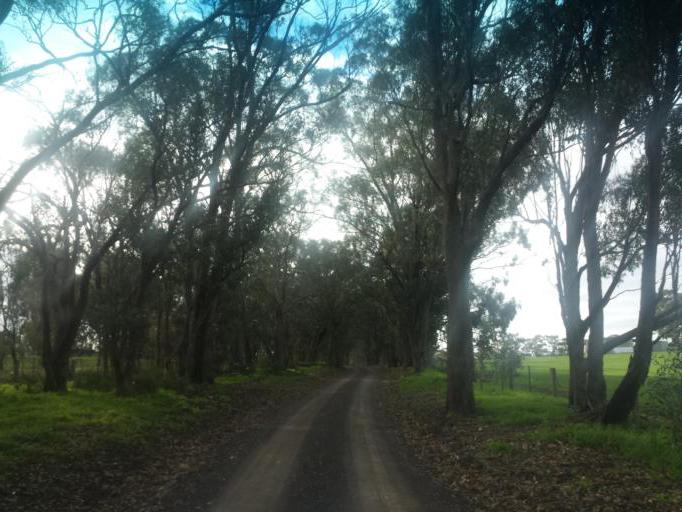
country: AU
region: Victoria
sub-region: Murrindindi
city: Kinglake West
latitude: -37.0272
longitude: 145.2502
